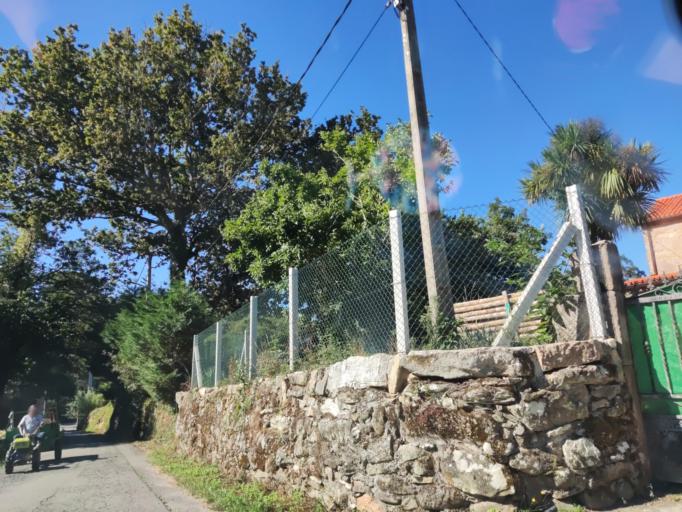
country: ES
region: Galicia
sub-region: Provincia da Coruna
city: Rianxo
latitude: 42.6900
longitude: -8.8471
